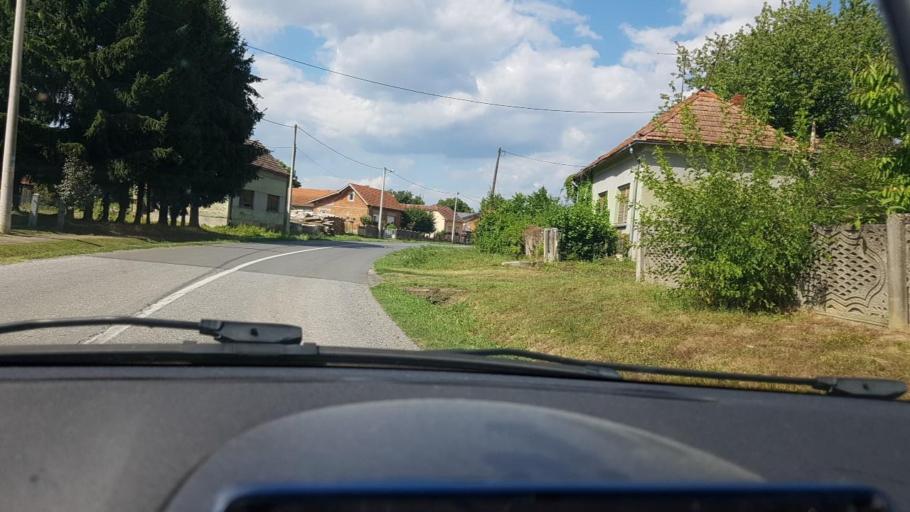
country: HR
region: Bjelovarsko-Bilogorska
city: Zdralovi
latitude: 45.8455
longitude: 16.9733
